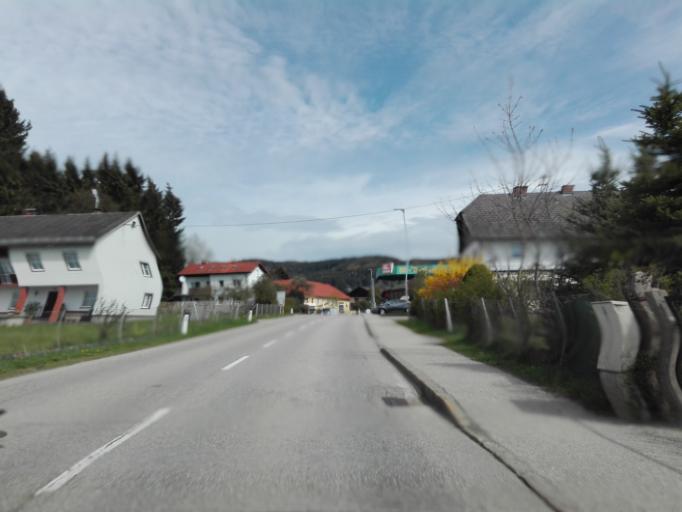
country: AT
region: Upper Austria
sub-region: Politischer Bezirk Urfahr-Umgebung
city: Eidenberg
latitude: 48.3607
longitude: 14.2399
